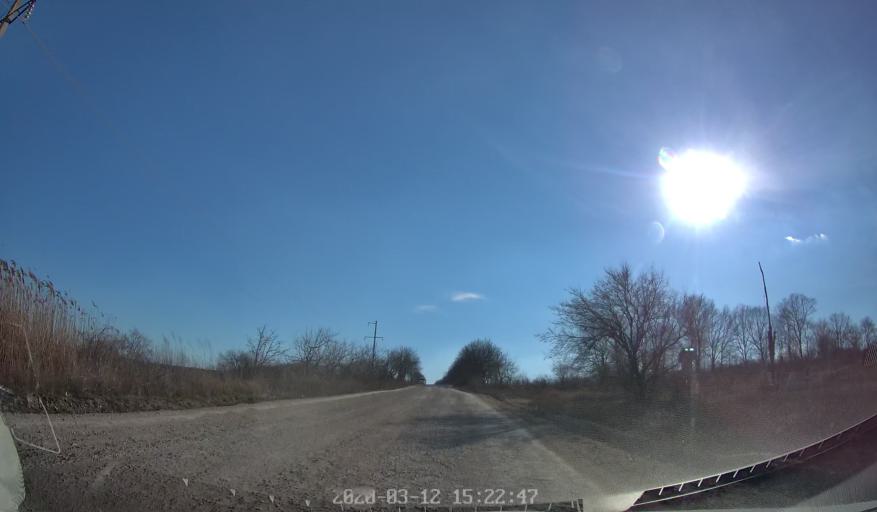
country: MD
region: Chisinau
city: Ciorescu
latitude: 47.1951
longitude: 28.9188
